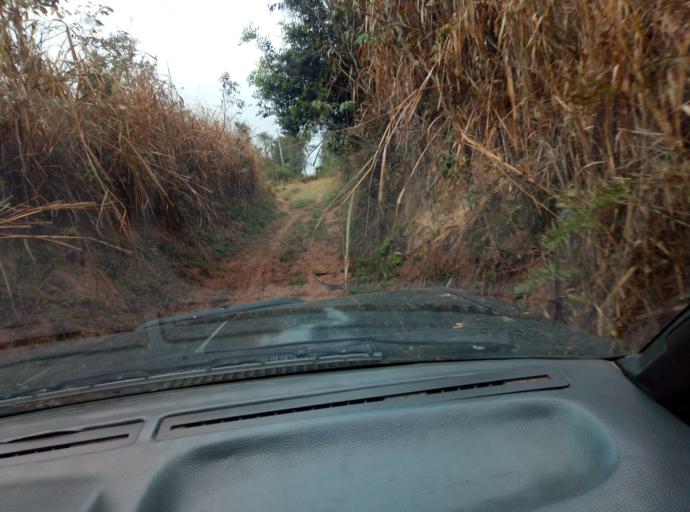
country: PY
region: Caaguazu
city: Carayao
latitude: -25.1971
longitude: -56.3544
